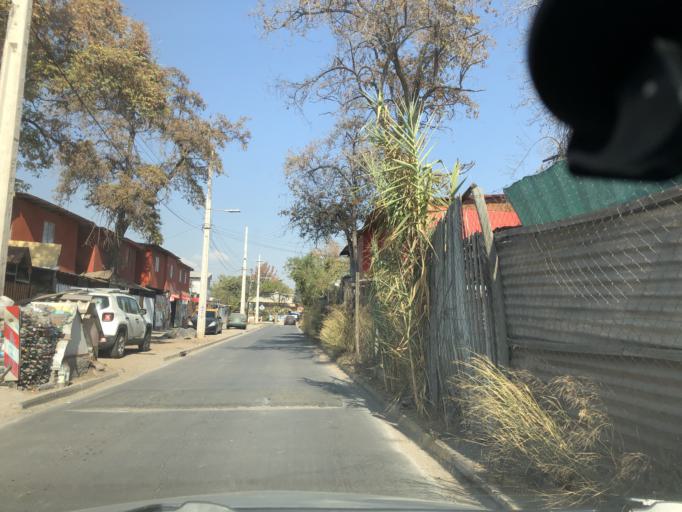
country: CL
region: Santiago Metropolitan
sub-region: Provincia de Cordillera
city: Puente Alto
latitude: -33.6056
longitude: -70.5645
